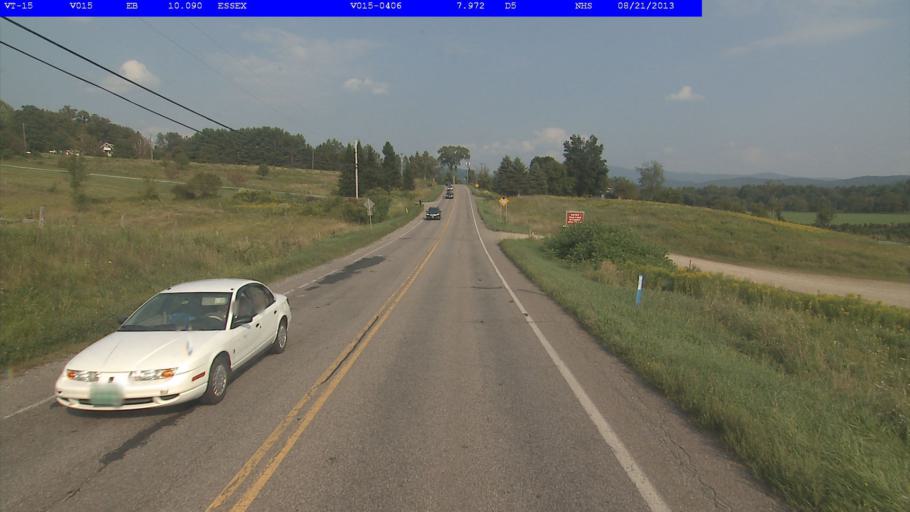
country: US
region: Vermont
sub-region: Chittenden County
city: Jericho
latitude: 44.5031
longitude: -73.0097
